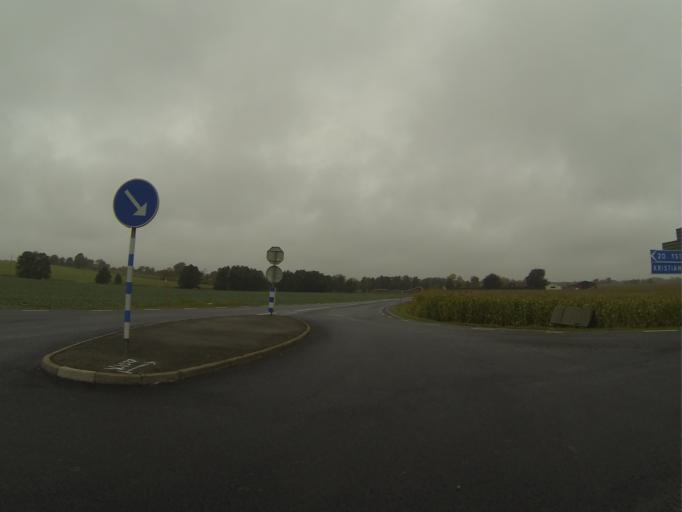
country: SE
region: Skane
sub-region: Tomelilla Kommun
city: Tomelilla
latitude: 55.5730
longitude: 13.9289
